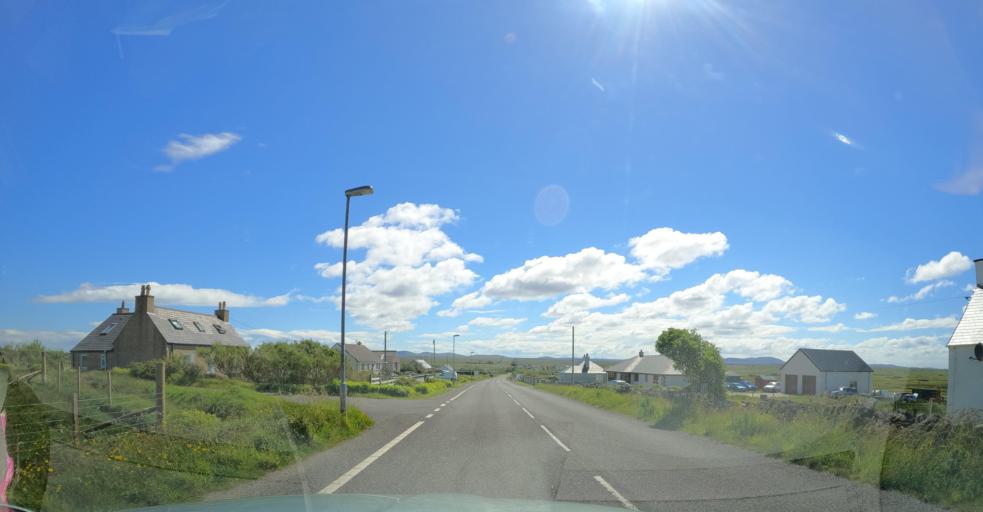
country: GB
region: Scotland
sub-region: Eilean Siar
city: Isle of Lewis
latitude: 58.3675
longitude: -6.5064
